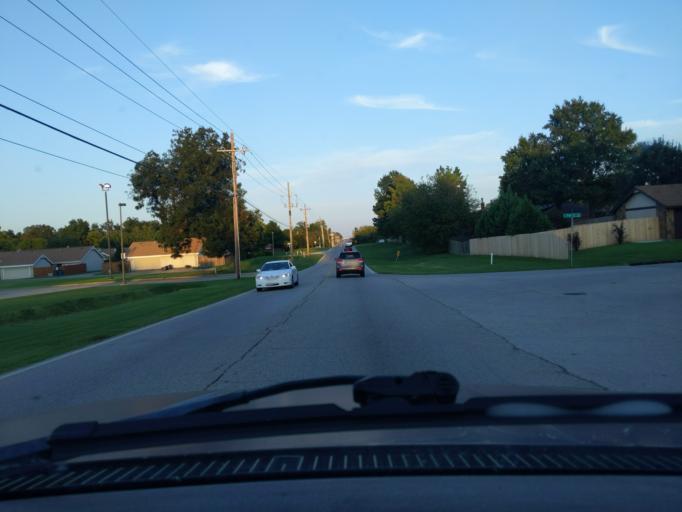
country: US
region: Oklahoma
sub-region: Tulsa County
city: Jenks
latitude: 36.0464
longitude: -95.8941
